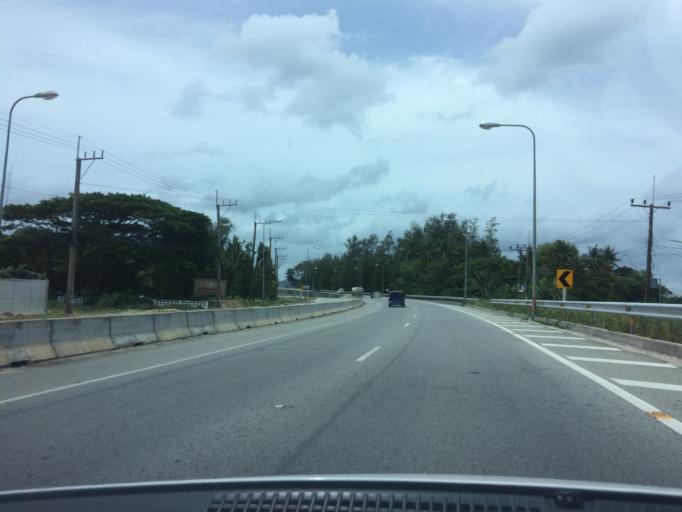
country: TH
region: Phuket
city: Thalang
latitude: 8.1963
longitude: 98.2947
